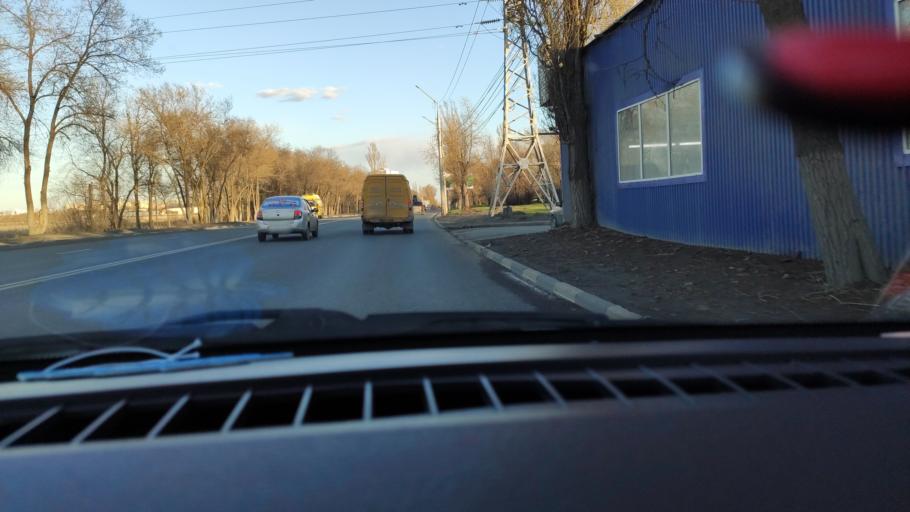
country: RU
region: Saratov
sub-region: Saratovskiy Rayon
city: Saratov
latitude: 51.5755
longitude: 45.9888
